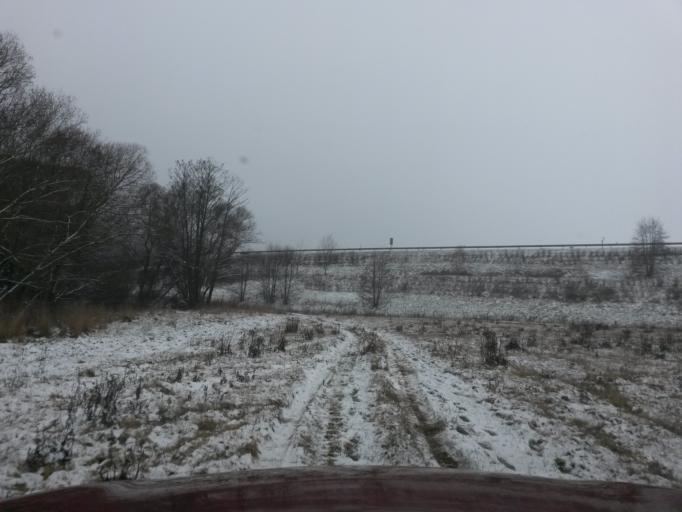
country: SK
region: Presovsky
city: Sabinov
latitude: 49.0006
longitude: 21.1114
